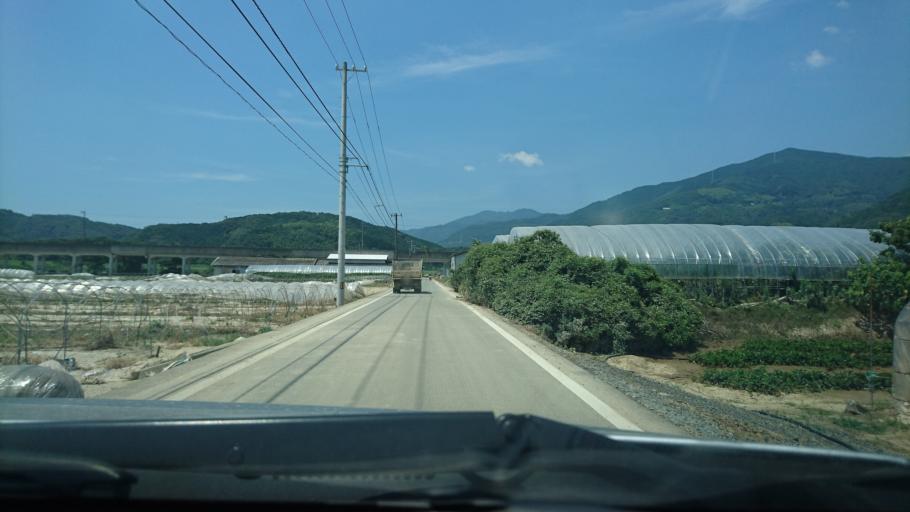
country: JP
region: Ehime
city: Ozu
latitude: 33.5319
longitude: 132.5680
